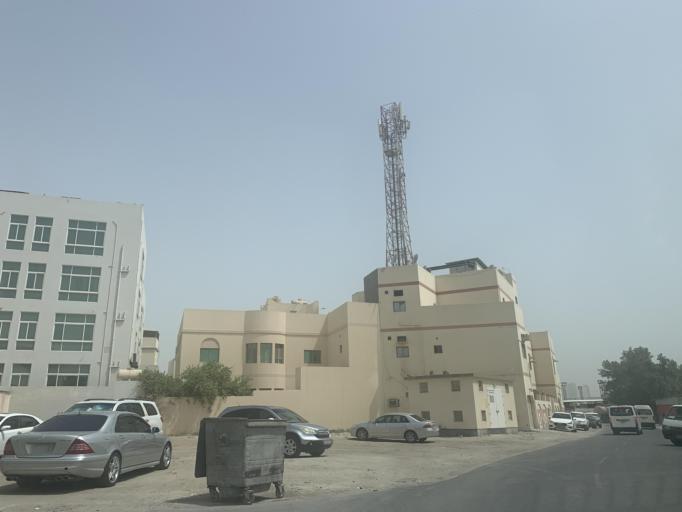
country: BH
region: Manama
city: Jidd Hafs
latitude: 26.2126
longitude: 50.5452
